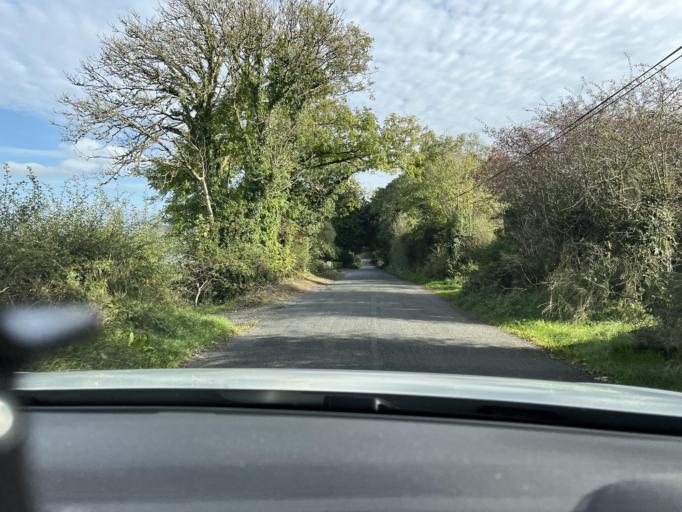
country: IE
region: Connaught
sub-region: Sligo
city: Ballymote
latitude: 54.0841
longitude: -8.4349
